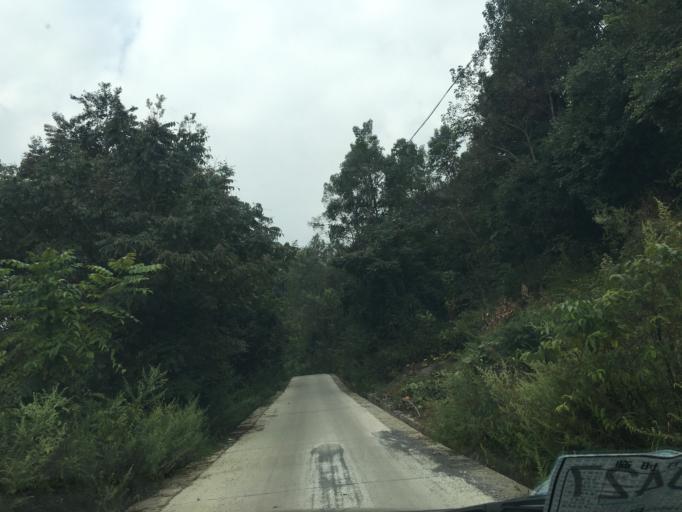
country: CN
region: Guangxi Zhuangzu Zizhiqu
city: Xinzhou
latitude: 25.5644
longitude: 105.6026
